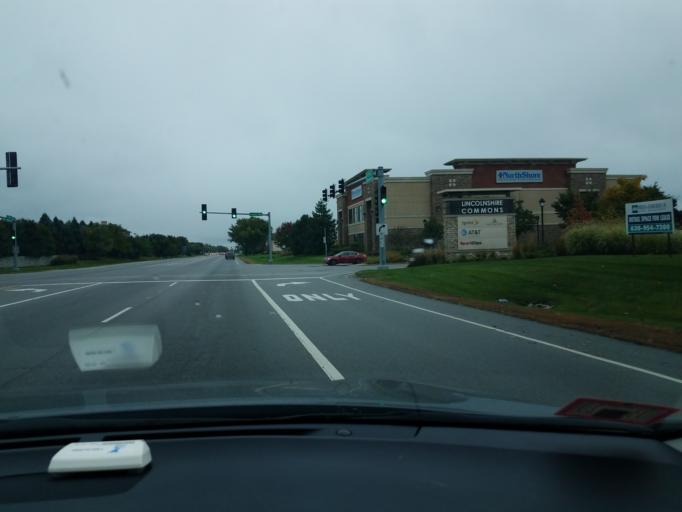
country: US
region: Illinois
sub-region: Lake County
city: Lincolnshire
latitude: 42.1846
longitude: -87.9273
